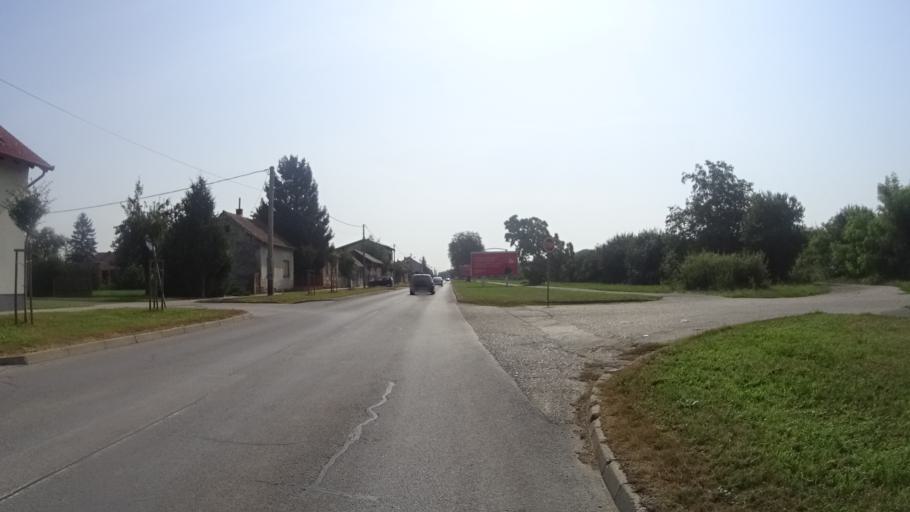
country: HR
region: Medimurska
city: Mihovljan
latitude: 46.3931
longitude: 16.4552
